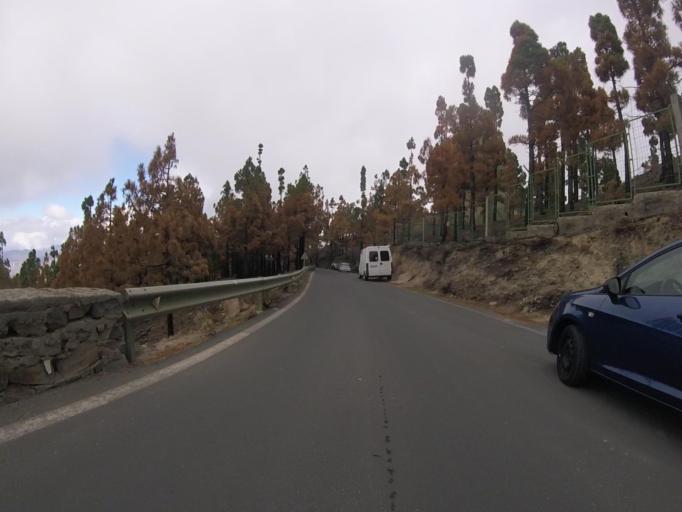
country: ES
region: Canary Islands
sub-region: Provincia de Las Palmas
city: San Bartolome
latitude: 27.9622
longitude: -15.5720
